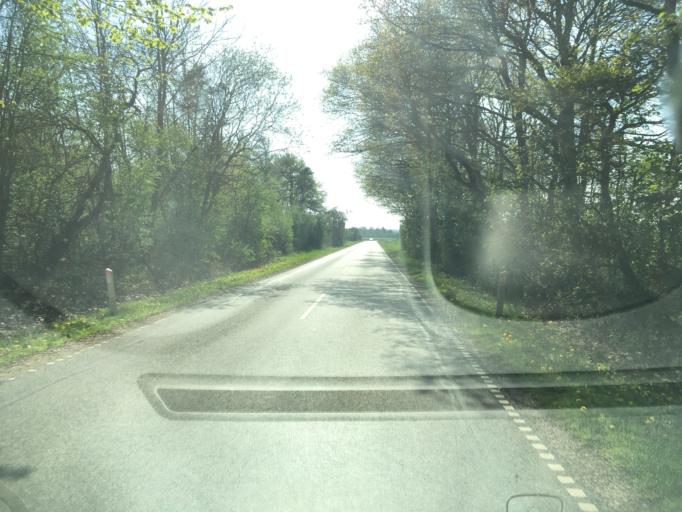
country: DK
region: South Denmark
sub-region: Haderslev Kommune
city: Vojens
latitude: 55.2865
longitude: 9.2232
